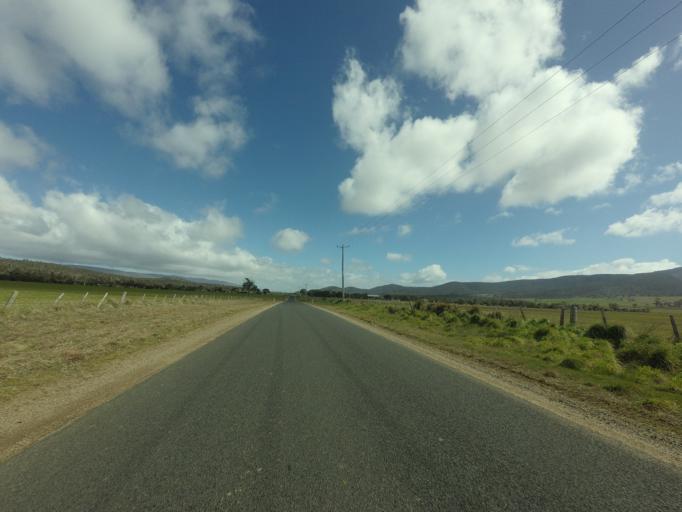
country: AU
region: Tasmania
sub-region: Northern Midlands
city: Evandale
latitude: -41.8247
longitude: 147.8373
